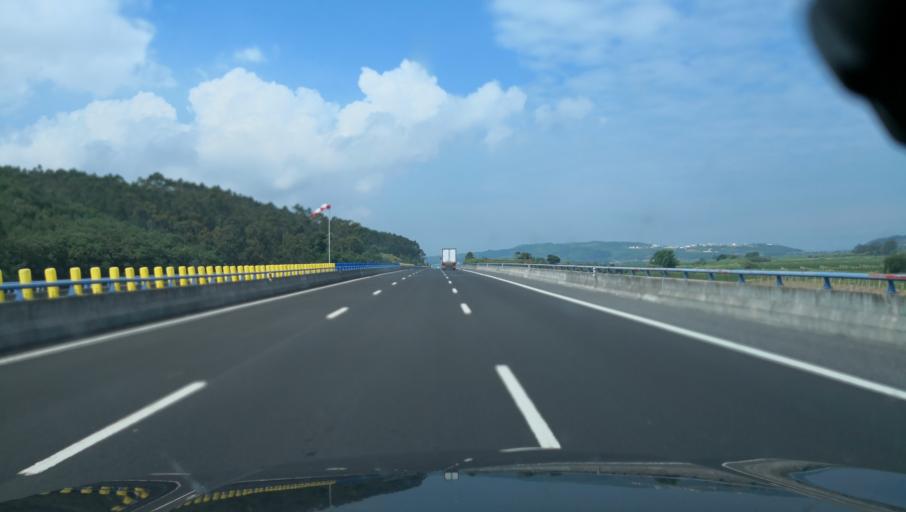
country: PT
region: Leiria
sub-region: Nazare
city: Nazare
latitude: 39.5792
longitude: -9.0251
